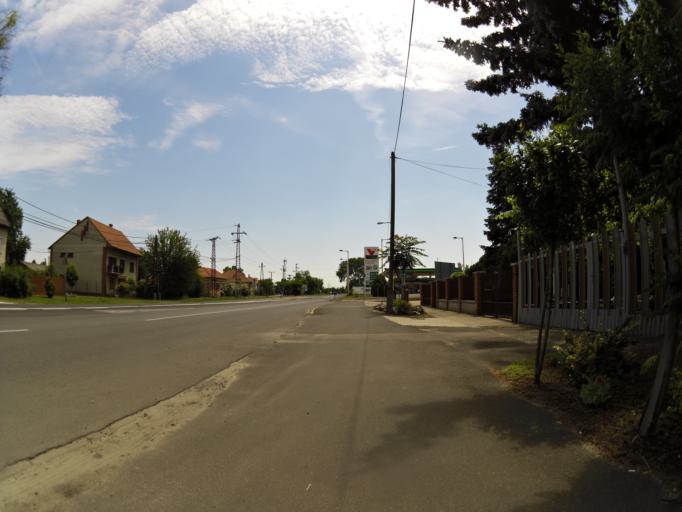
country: HU
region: Csongrad
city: Kistelek
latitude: 46.4635
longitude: 19.9855
